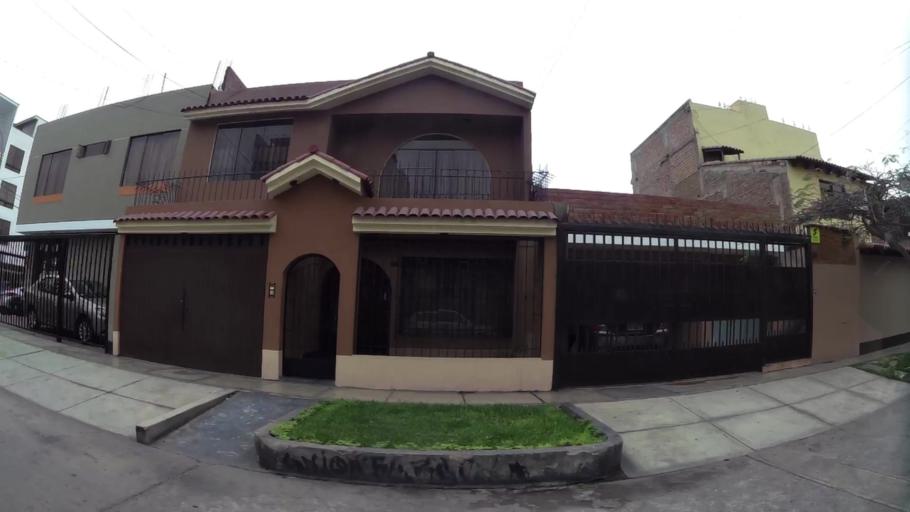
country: PE
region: Lima
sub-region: Lima
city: Surco
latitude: -12.1403
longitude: -76.9869
